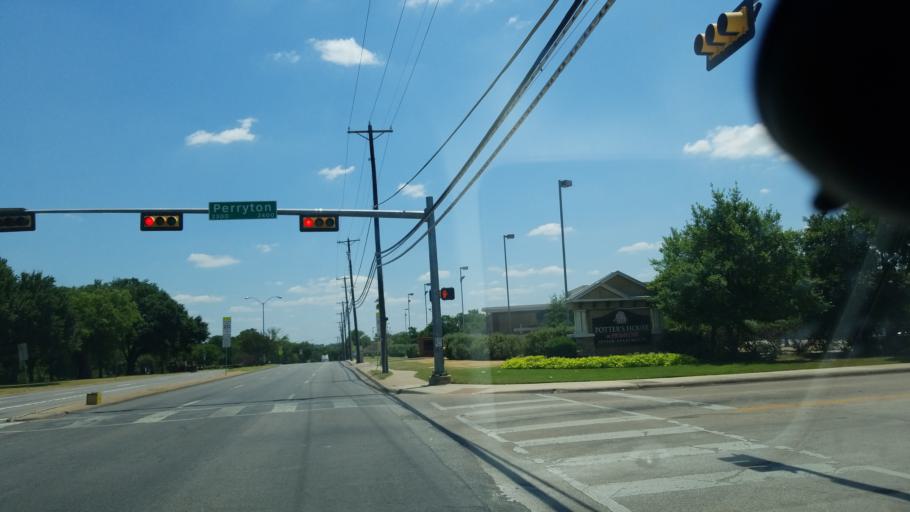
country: US
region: Texas
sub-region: Dallas County
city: Cockrell Hill
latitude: 32.7142
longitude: -96.8572
